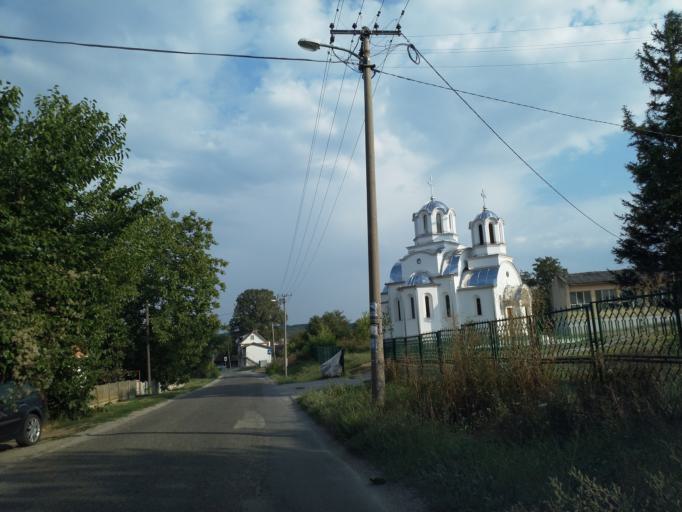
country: RS
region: Central Serbia
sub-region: Pomoravski Okrug
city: Paracin
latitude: 43.8424
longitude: 21.4722
